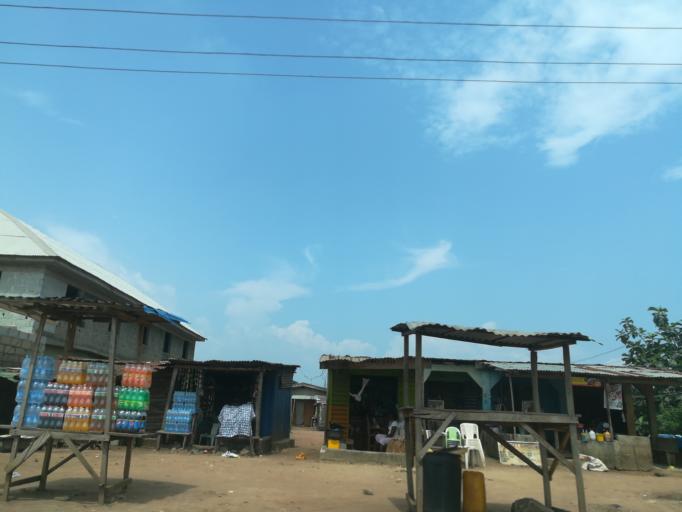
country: NG
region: Lagos
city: Ikorodu
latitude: 6.5867
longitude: 3.6249
